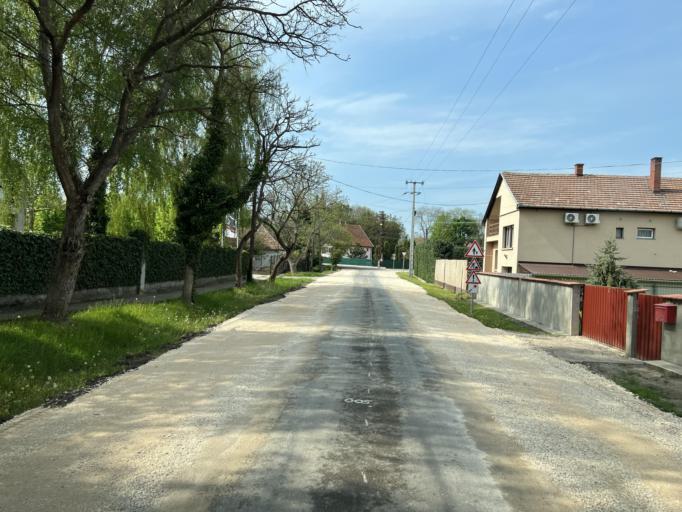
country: HU
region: Pest
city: Tapioszele
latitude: 47.3344
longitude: 19.8748
